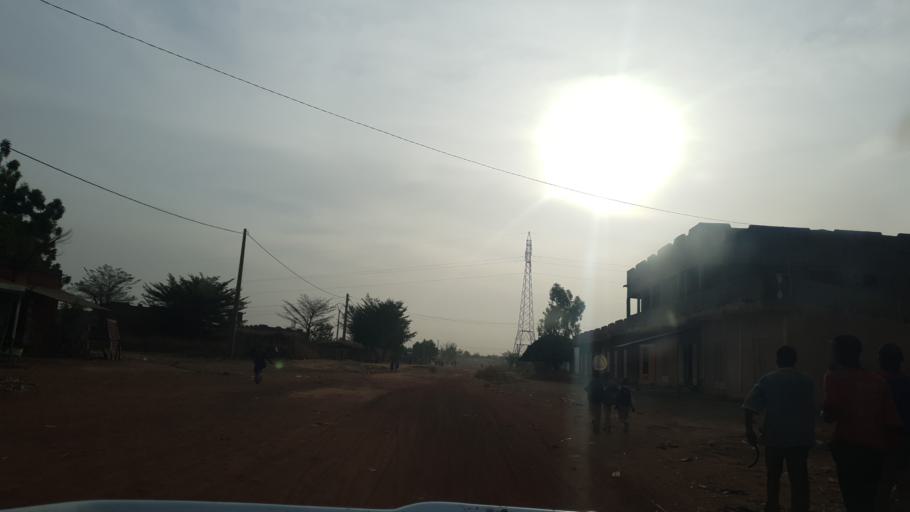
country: ML
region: Segou
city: Baroueli
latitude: 12.7753
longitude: -6.9411
